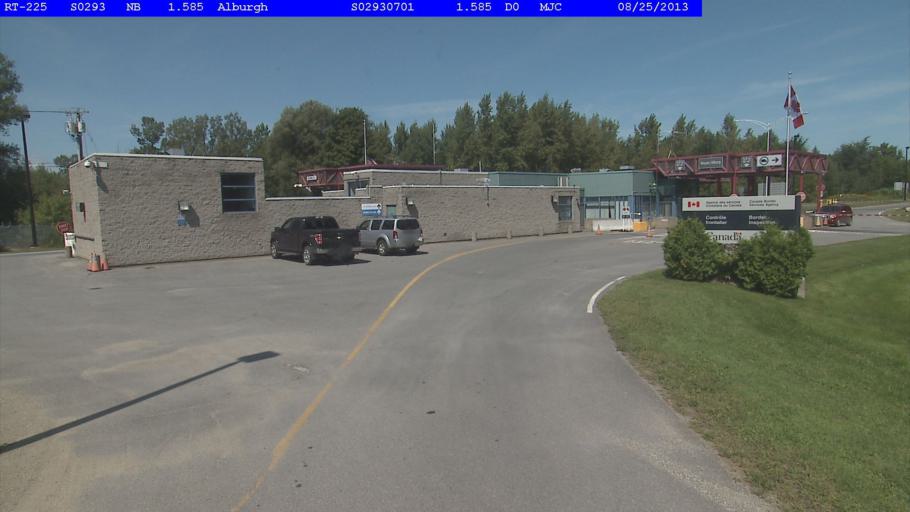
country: US
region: New York
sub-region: Clinton County
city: Rouses Point
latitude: 45.0112
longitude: -73.2963
